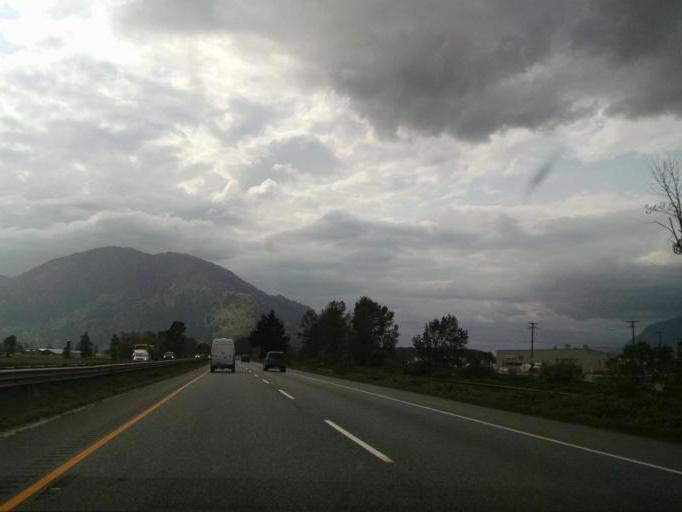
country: CA
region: British Columbia
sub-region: Fraser Valley Regional District
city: Chilliwack
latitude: 49.1398
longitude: -122.0488
